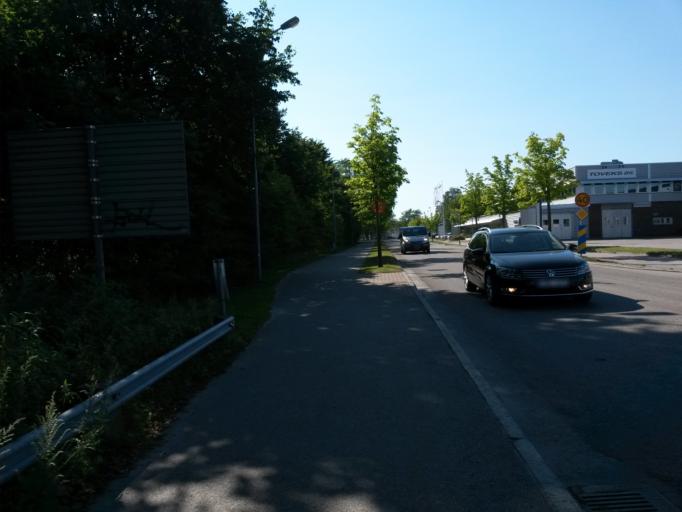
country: SE
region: Vaestra Goetaland
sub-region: Lidkopings Kommun
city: Lidkoping
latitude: 58.4969
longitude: 13.1793
